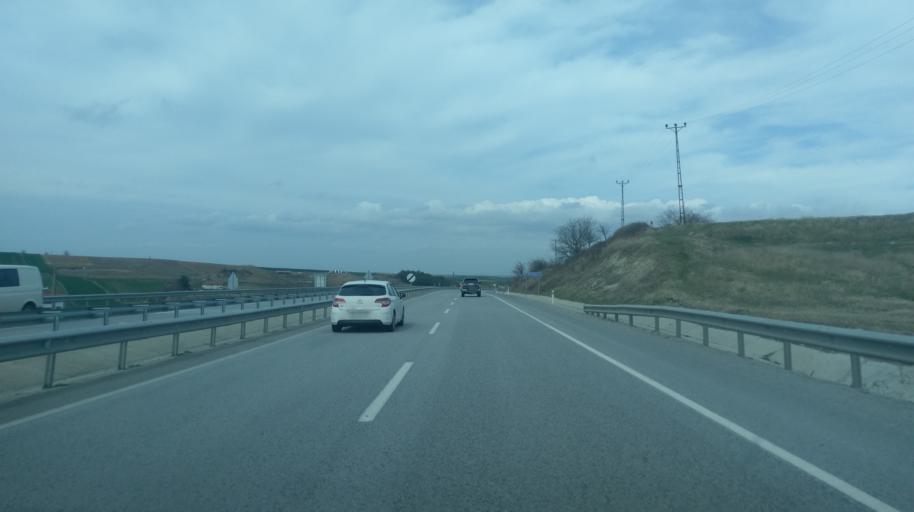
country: TR
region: Edirne
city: Kircasalih
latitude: 41.3989
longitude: 26.8095
